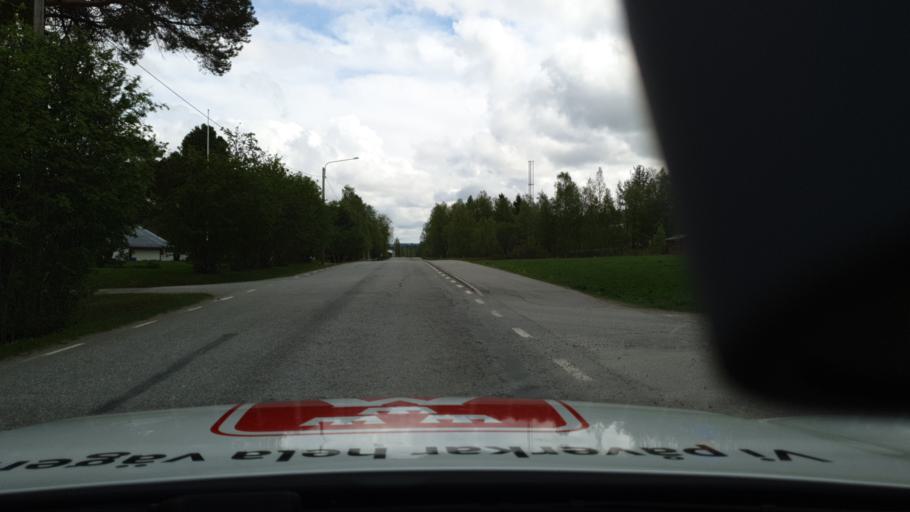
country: SE
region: Vaesterbotten
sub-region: Vilhelmina Kommun
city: Sjoberg
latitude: 64.6380
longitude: 16.3648
